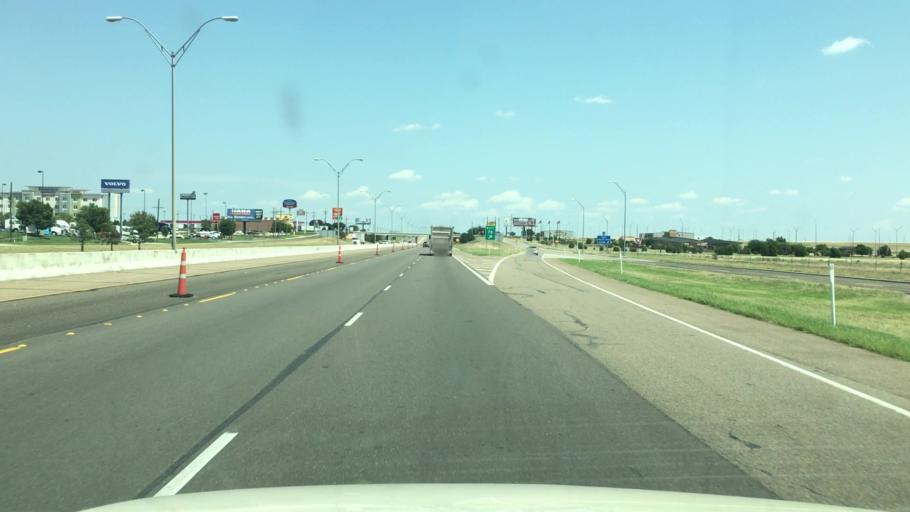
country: US
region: Texas
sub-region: Potter County
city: Amarillo
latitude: 35.1927
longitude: -101.7306
